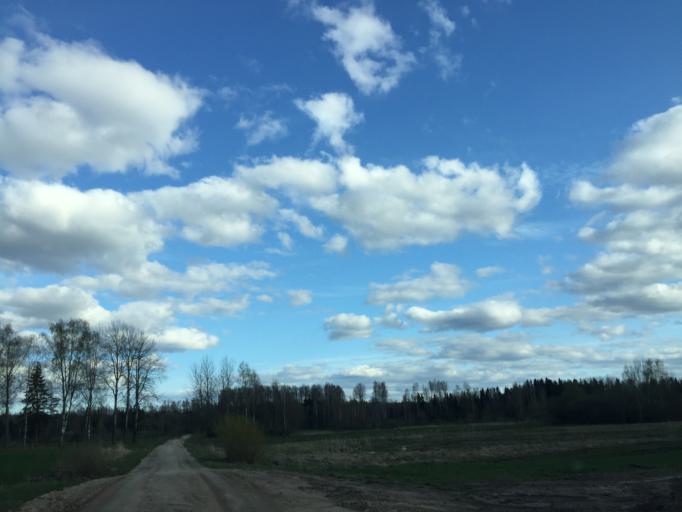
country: LV
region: Karsava
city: Karsava
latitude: 56.6777
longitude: 27.5254
